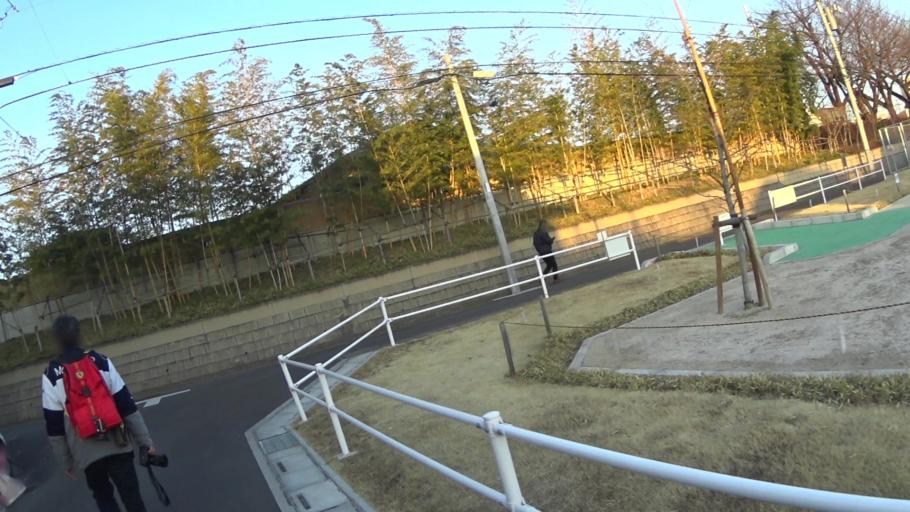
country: JP
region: Saitama
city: Saitama
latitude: 35.9283
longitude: 139.6338
